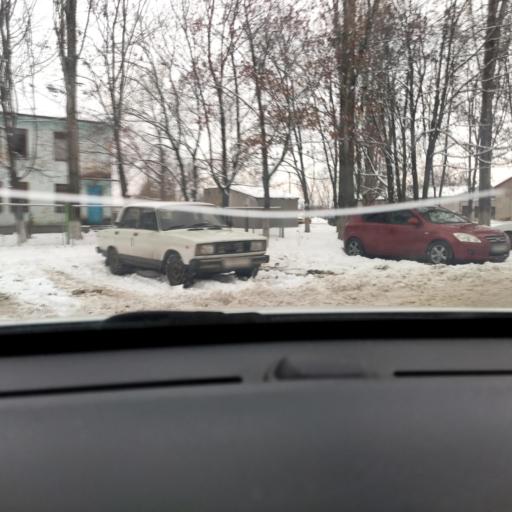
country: RU
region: Voronezj
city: Novaya Usman'
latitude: 51.6480
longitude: 39.4162
